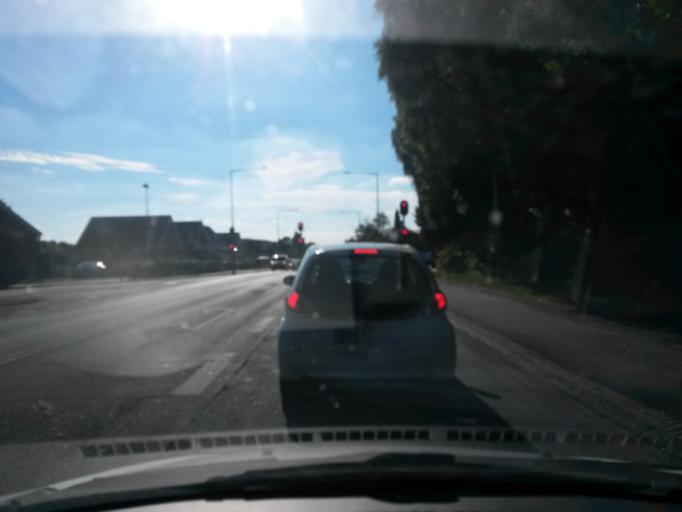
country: DK
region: Central Jutland
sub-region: Silkeborg Kommune
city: Silkeborg
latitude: 56.1780
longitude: 9.5304
